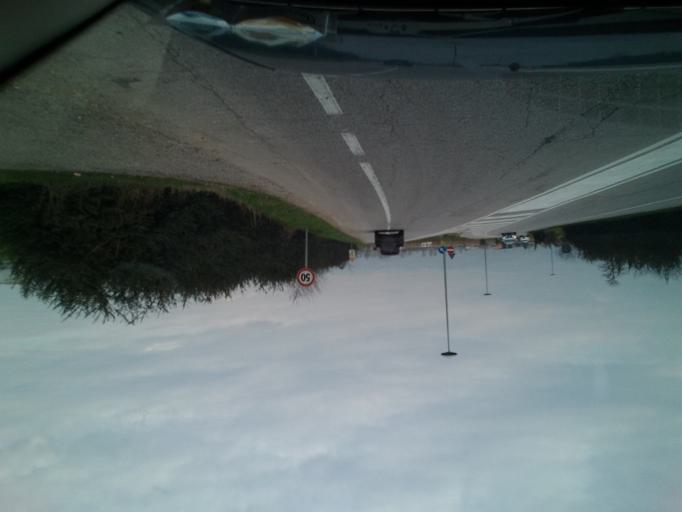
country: IT
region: Veneto
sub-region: Provincia di Verona
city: Sona
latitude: 45.4368
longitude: 10.8499
